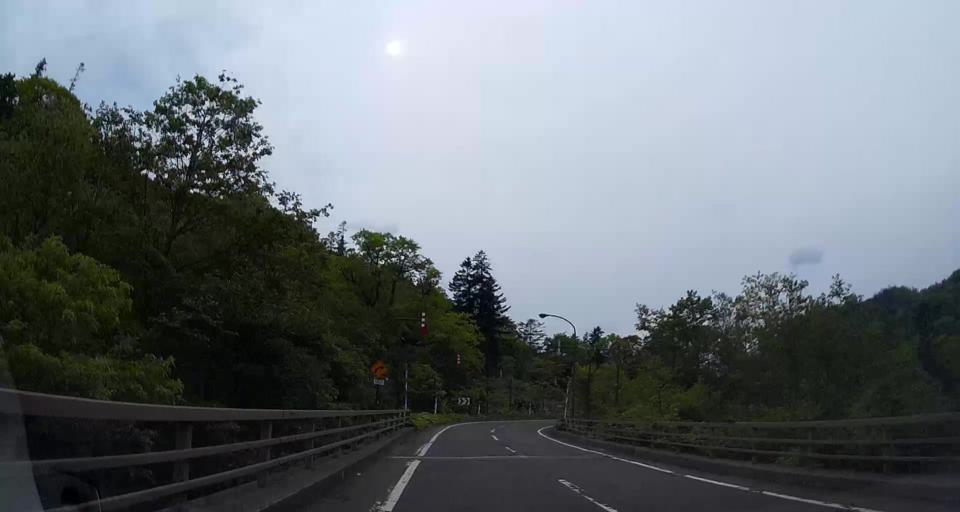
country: JP
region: Hokkaido
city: Shiraoi
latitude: 42.6468
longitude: 141.2160
